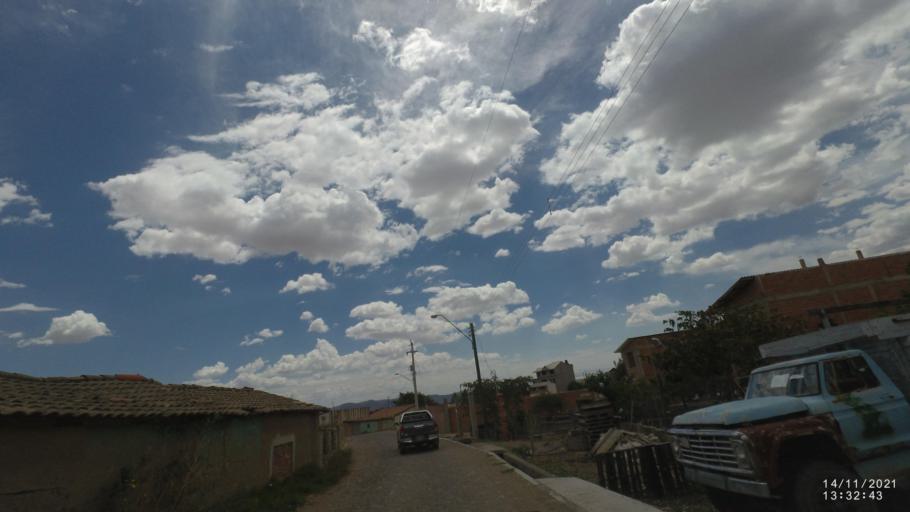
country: BO
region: Cochabamba
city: Colomi
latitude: -17.3971
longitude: -65.9843
